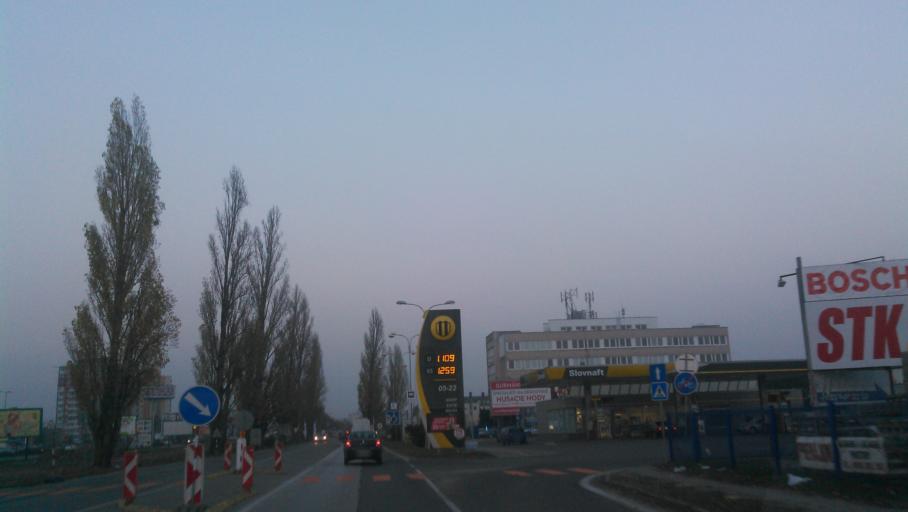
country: SK
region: Bratislavsky
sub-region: Okres Pezinok
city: Pezinok
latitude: 48.2762
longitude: 17.2555
